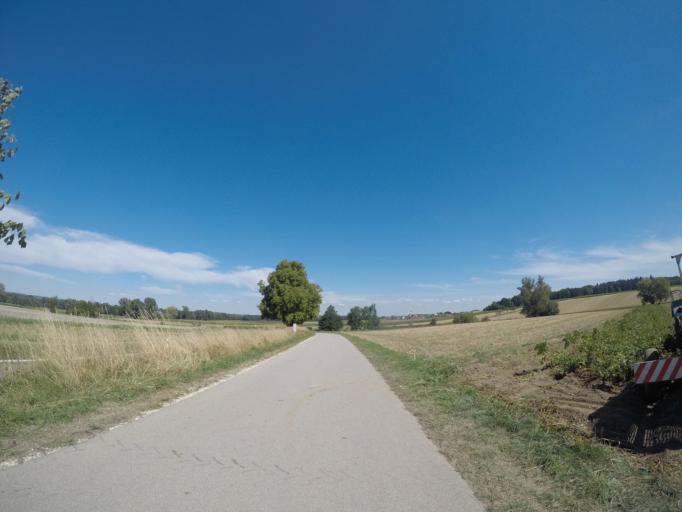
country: DE
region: Bavaria
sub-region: Swabia
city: Holzheim
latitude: 48.3674
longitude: 10.0706
